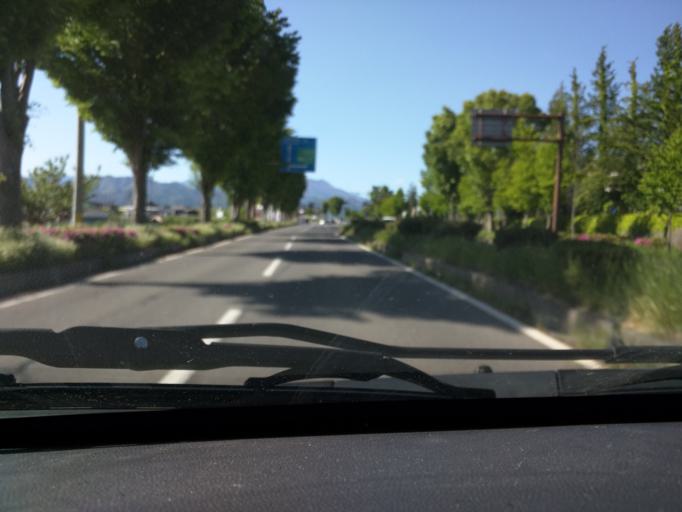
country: JP
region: Nagano
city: Nagano-shi
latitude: 36.5760
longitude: 138.1981
